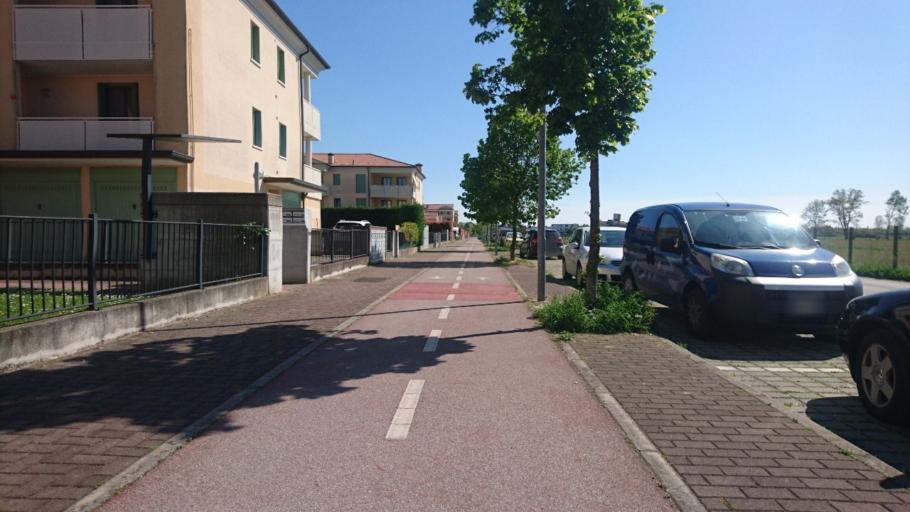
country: IT
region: Veneto
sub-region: Provincia di Venezia
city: Marcon-Gaggio-Colmello
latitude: 45.5611
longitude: 12.2944
